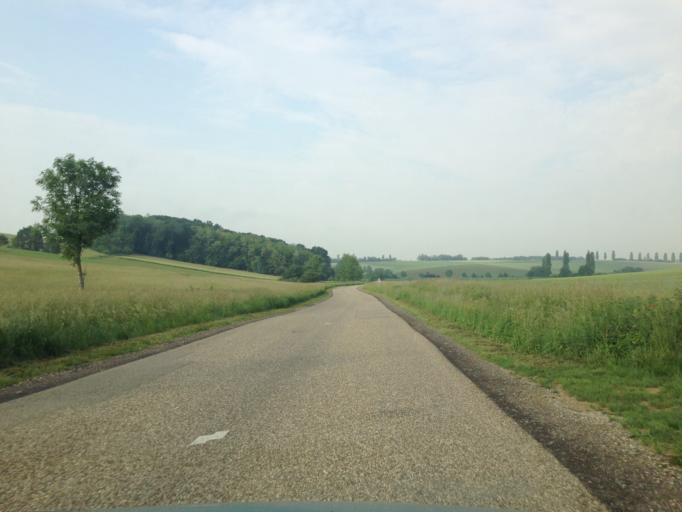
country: FR
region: Alsace
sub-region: Departement du Bas-Rhin
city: Hochfelden
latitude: 48.7775
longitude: 7.5788
